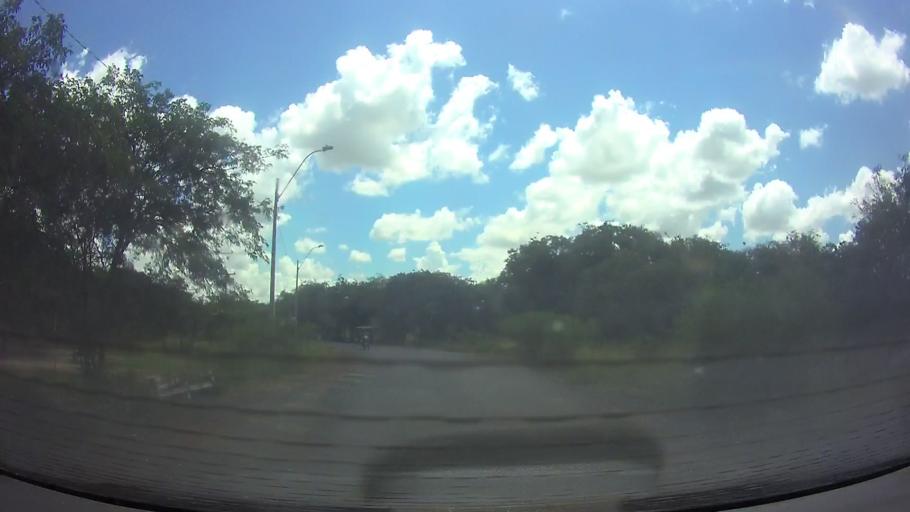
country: PY
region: Presidente Hayes
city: Nanawa
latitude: -25.2436
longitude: -57.6776
